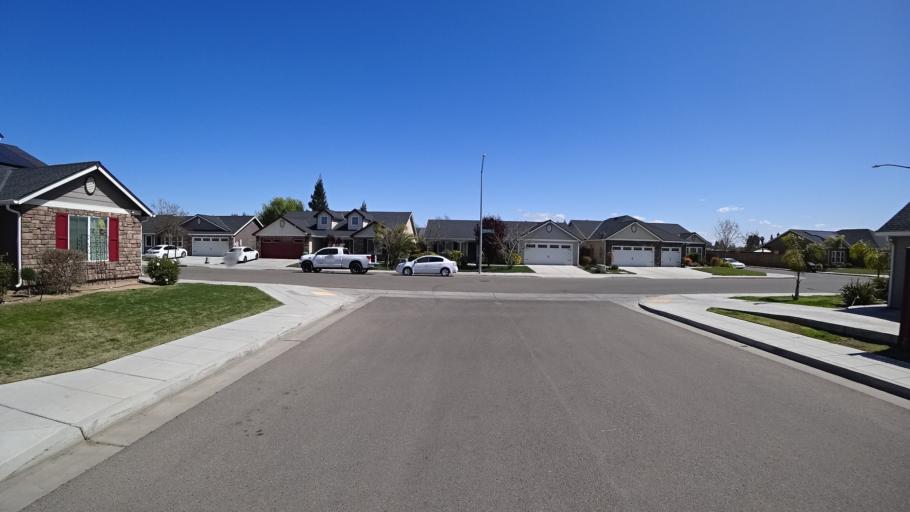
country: US
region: California
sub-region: Fresno County
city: West Park
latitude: 36.7743
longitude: -119.8855
